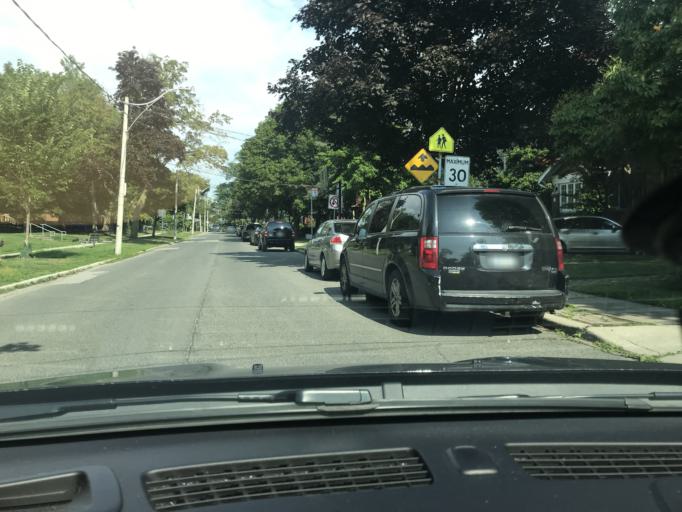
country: CA
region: Ontario
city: Toronto
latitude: 43.7178
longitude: -79.4093
